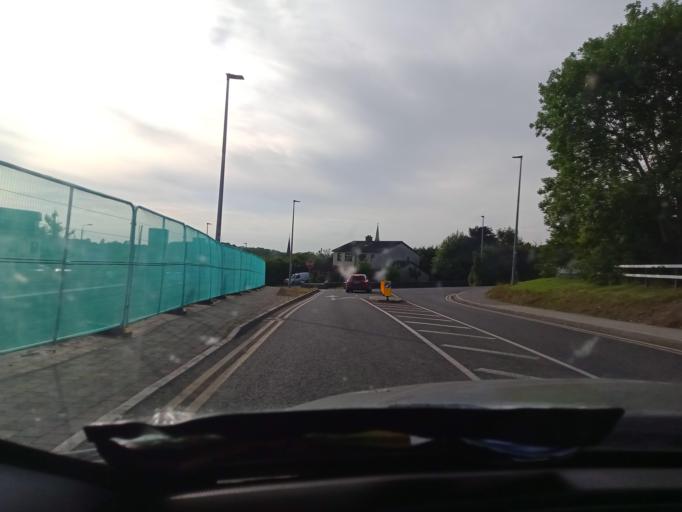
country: IE
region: Ulster
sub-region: An Cabhan
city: Cavan
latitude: 53.9925
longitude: -7.3560
